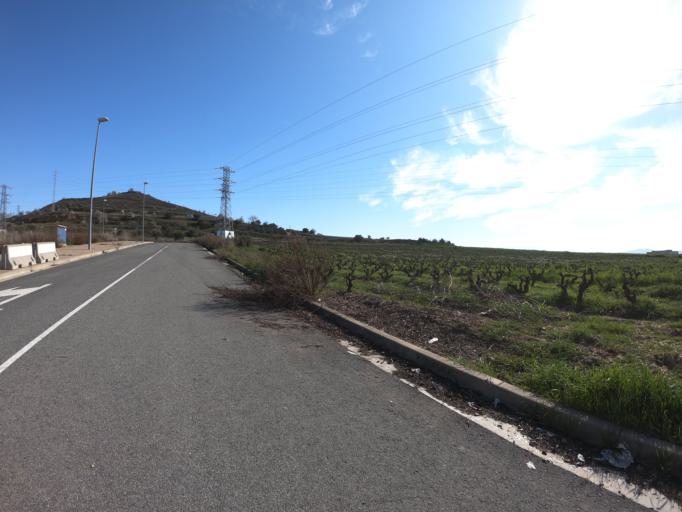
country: ES
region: Basque Country
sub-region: Provincia de Alava
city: Oyon
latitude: 42.4845
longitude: -2.4345
